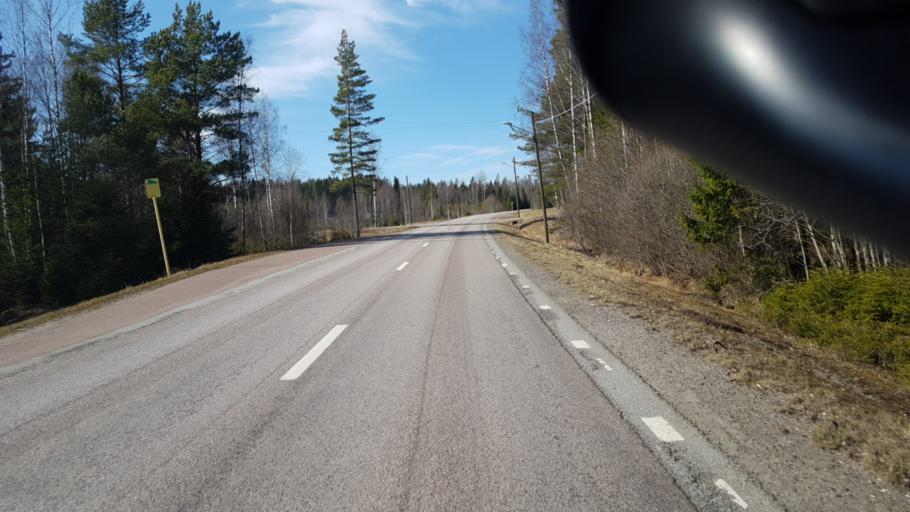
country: SE
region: Vaermland
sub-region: Arvika Kommun
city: Arvika
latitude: 59.6390
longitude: 12.7881
